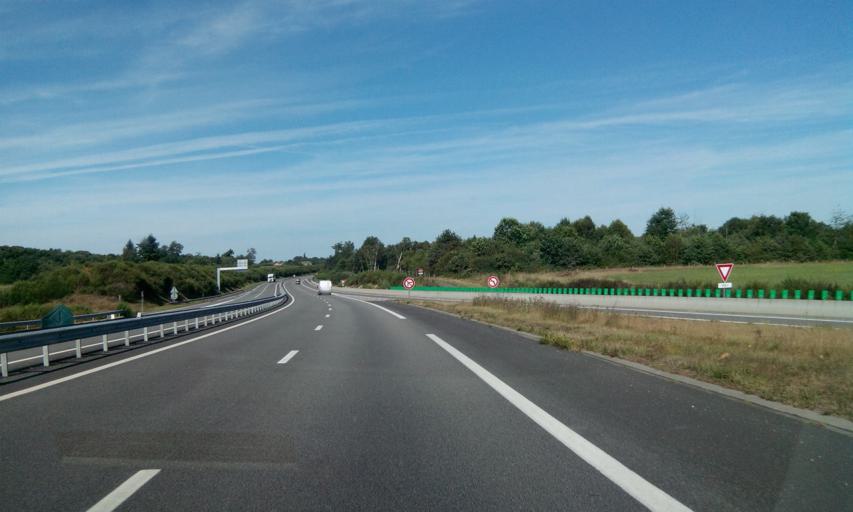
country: FR
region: Limousin
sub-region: Departement de la Haute-Vienne
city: Veyrac
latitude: 45.8833
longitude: 1.0946
